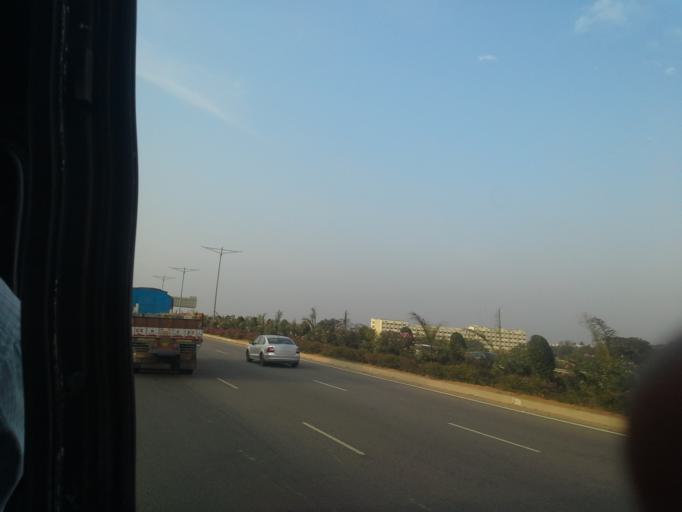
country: IN
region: Telangana
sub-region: Hyderabad
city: Hyderabad
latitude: 17.3370
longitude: 78.3674
